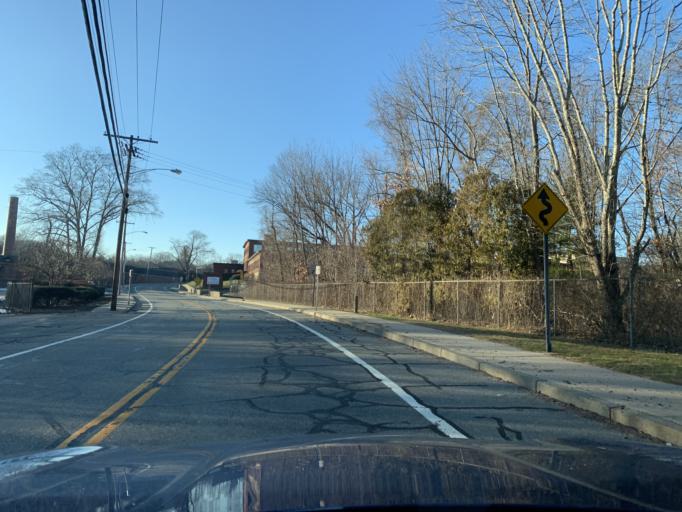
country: US
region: Rhode Island
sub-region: Kent County
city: West Warwick
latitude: 41.7289
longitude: -71.5416
